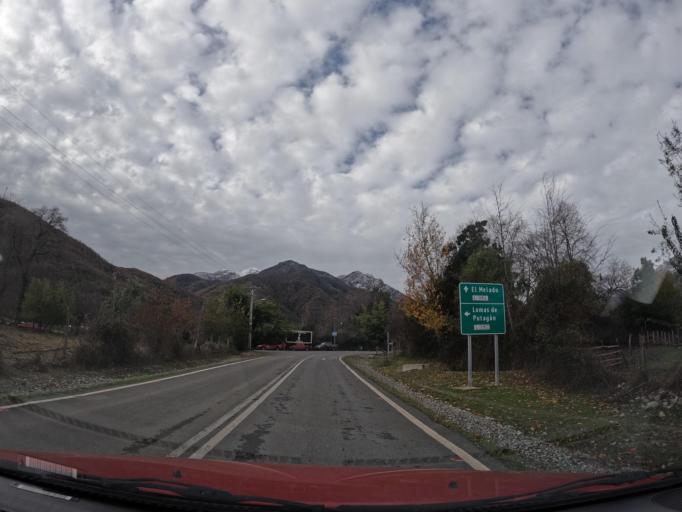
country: CL
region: Maule
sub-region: Provincia de Linares
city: Colbun
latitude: -35.8606
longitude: -71.2652
